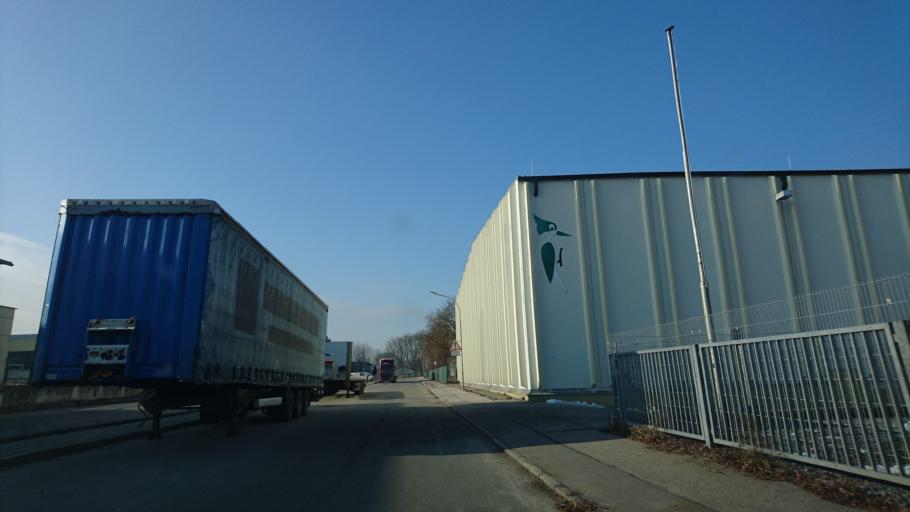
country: DE
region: Bavaria
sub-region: Lower Bavaria
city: Pfarrkirchen
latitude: 48.4216
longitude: 12.9392
